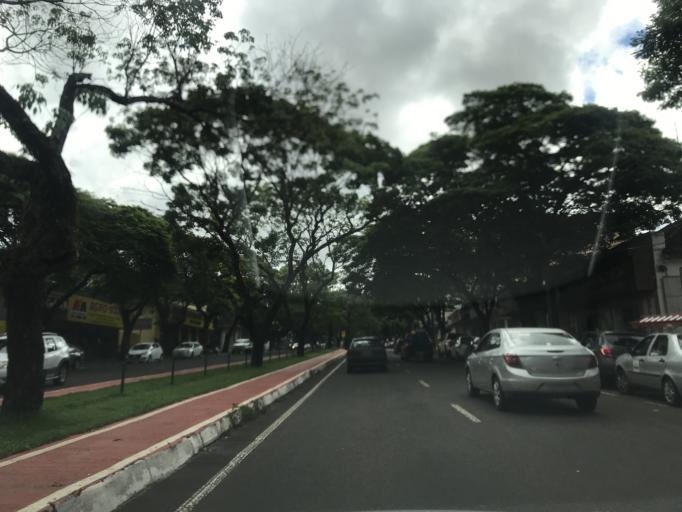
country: BR
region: Parana
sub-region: Maringa
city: Maringa
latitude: -23.4217
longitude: -51.9504
